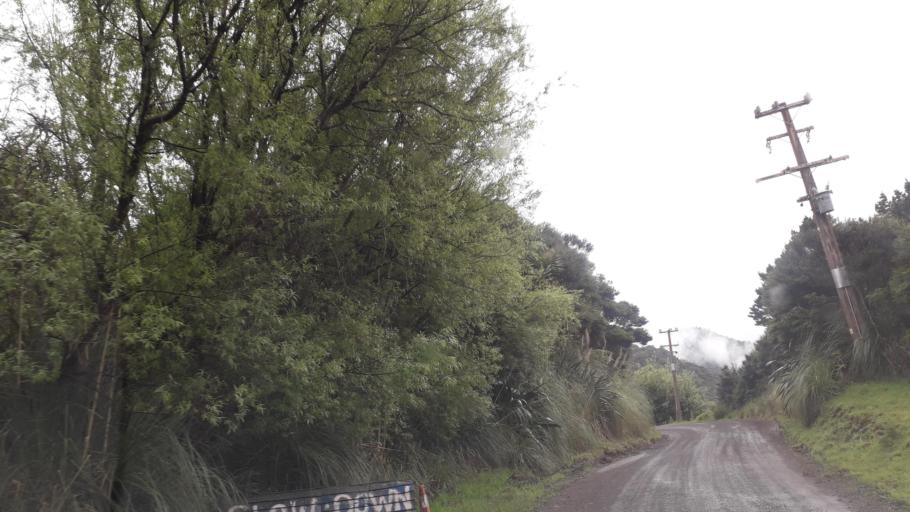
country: NZ
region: Northland
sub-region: Far North District
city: Ahipara
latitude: -35.4375
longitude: 173.3076
